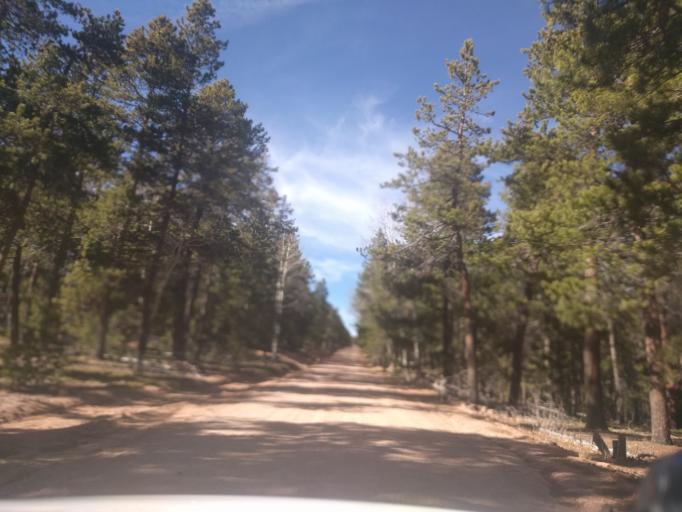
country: US
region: Colorado
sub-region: Douglas County
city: Perry Park
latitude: 39.1866
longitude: -105.0466
